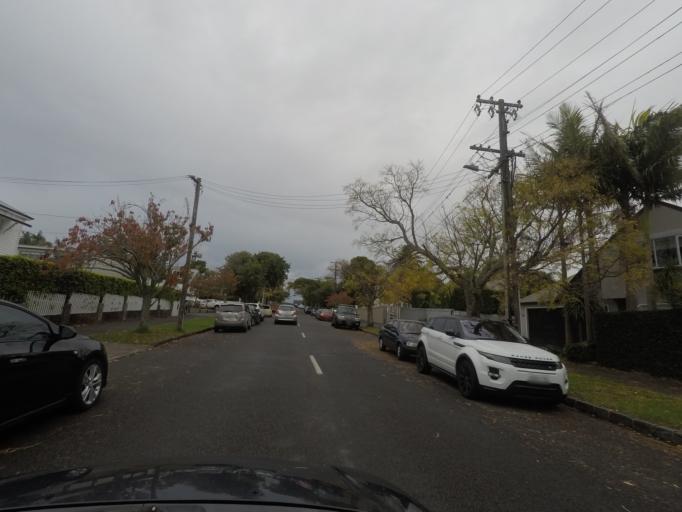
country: NZ
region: Auckland
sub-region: Auckland
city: Auckland
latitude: -36.8435
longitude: 174.7333
